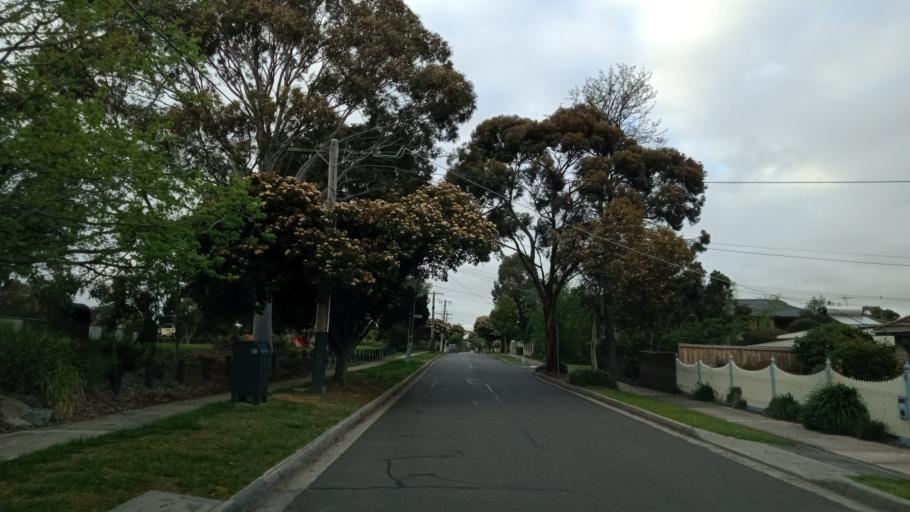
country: AU
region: Victoria
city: Burwood East
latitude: -37.8720
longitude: 145.1344
